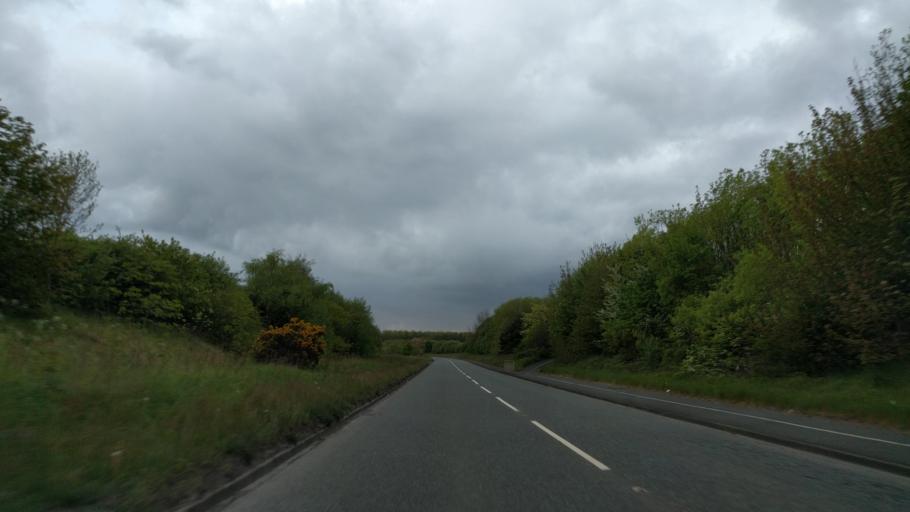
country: GB
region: England
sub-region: Northumberland
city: Newbiggin-by-the-Sea
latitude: 55.2000
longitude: -1.5278
